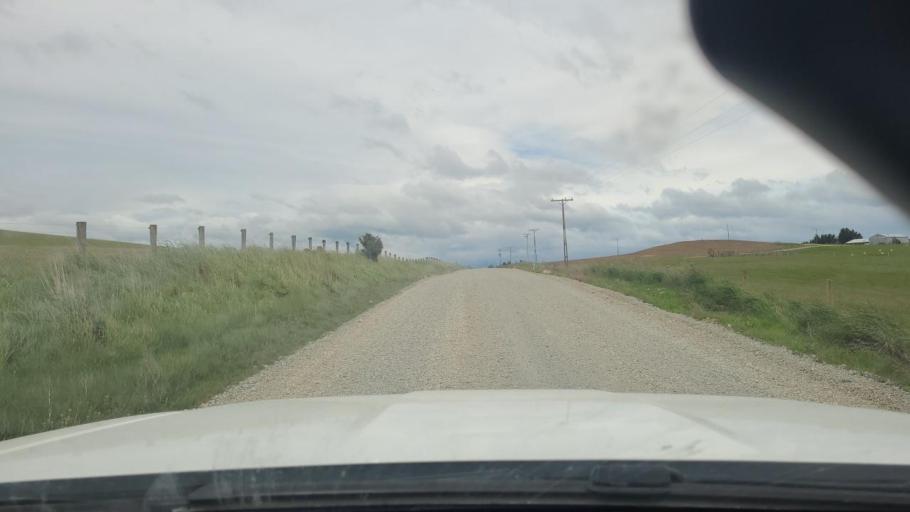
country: NZ
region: Southland
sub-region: Southland District
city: Te Anau
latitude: -45.4630
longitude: 167.8483
